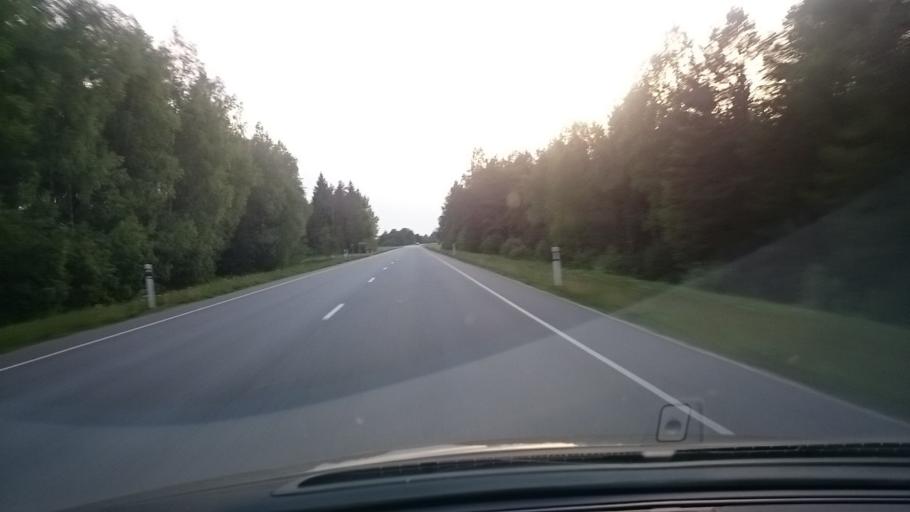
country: EE
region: Jaervamaa
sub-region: Tueri vald
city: Sarevere
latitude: 58.7651
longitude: 25.5378
